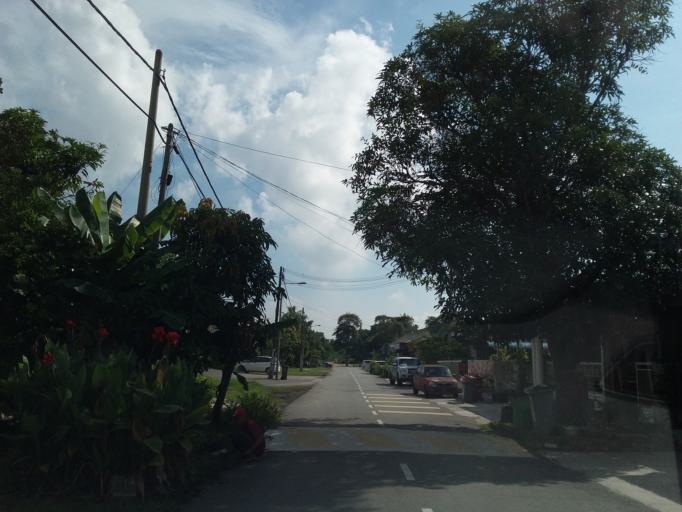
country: MY
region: Johor
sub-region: Daerah Batu Pahat
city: Batu Pahat
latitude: 1.8415
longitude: 102.9254
